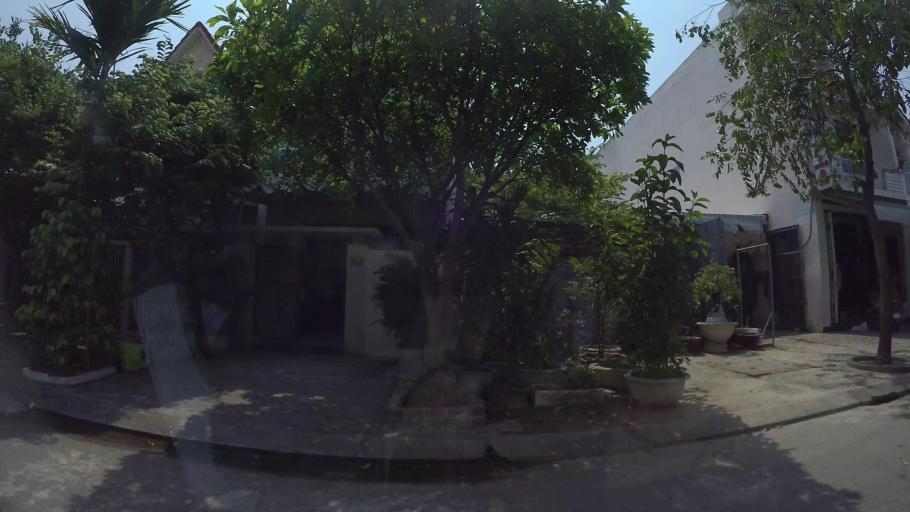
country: VN
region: Da Nang
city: Ngu Hanh Son
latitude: 16.0137
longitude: 108.2534
